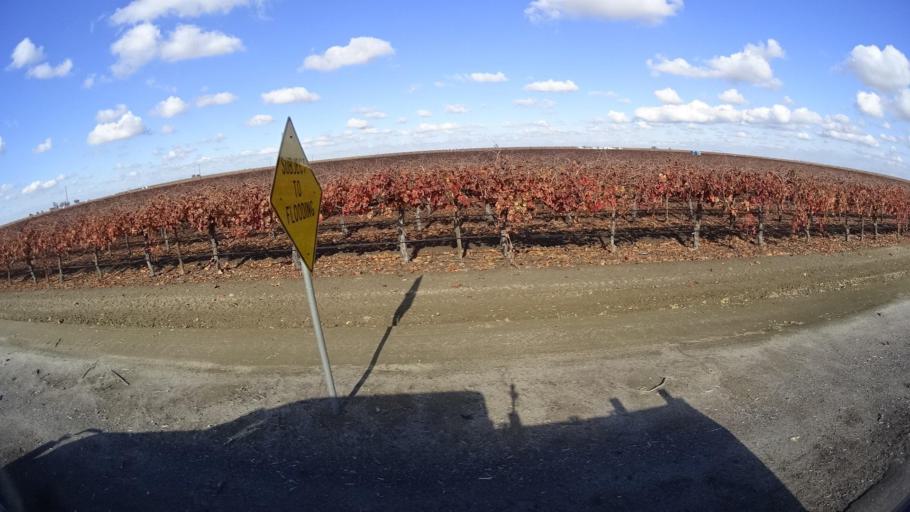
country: US
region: California
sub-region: Kern County
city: Delano
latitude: 35.7322
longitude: -119.3284
